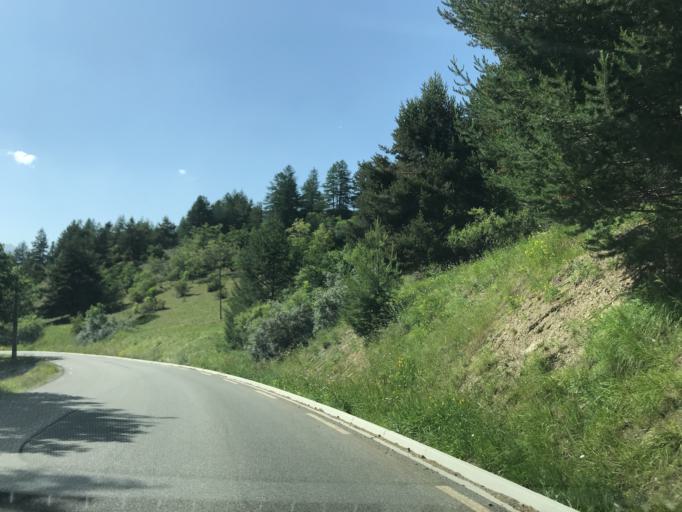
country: IT
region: Piedmont
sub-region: Provincia di Torino
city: Sauze di Cesana
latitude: 44.7525
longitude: 6.8290
